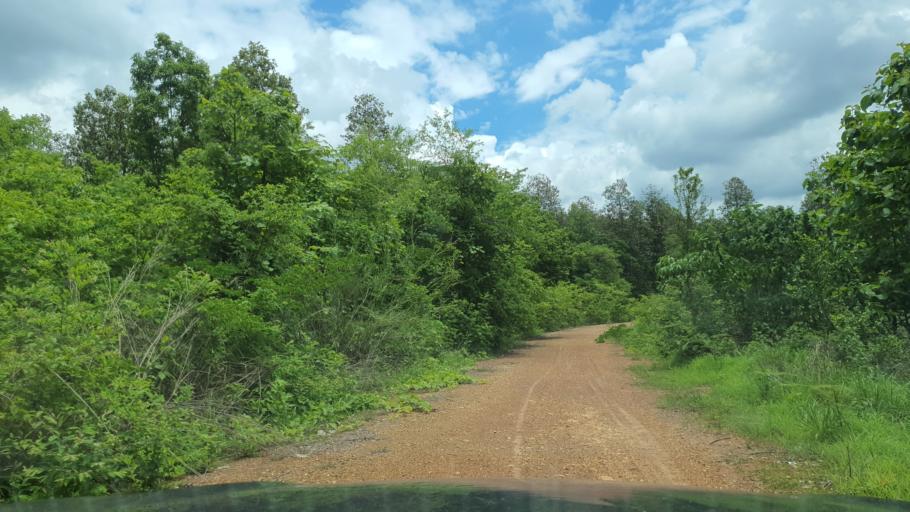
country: TH
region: Chiang Mai
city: San Sai
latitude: 18.9259
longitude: 99.0580
